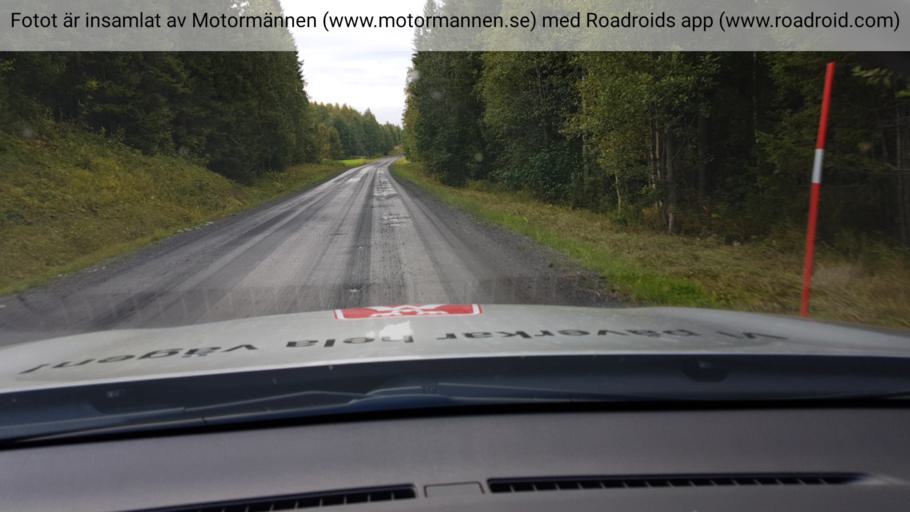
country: SE
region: Jaemtland
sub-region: Stroemsunds Kommun
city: Stroemsund
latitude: 64.1370
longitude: 15.7565
